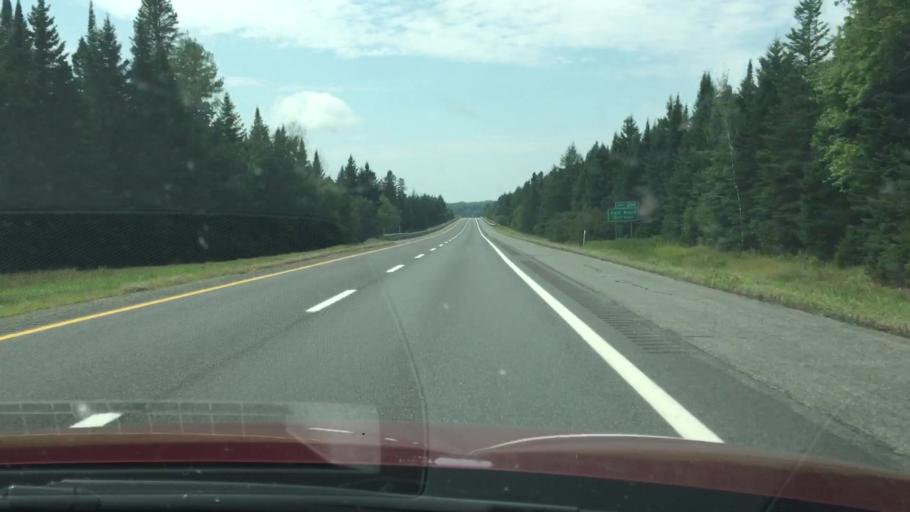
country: US
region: Maine
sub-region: Aroostook County
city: Hodgdon
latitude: 46.1149
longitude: -68.1412
